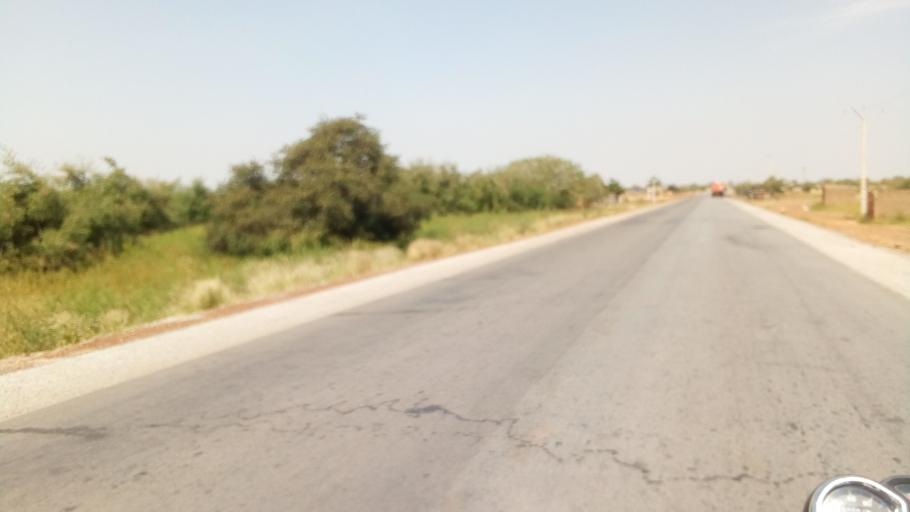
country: ML
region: Kayes
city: Kayes
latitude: 14.3952
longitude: -11.4614
